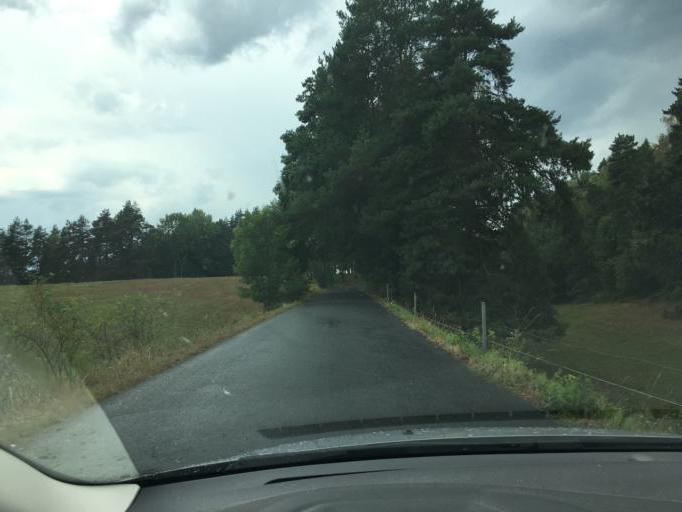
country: CZ
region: Ustecky
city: Ceska Kamenice
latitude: 50.8155
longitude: 14.3427
